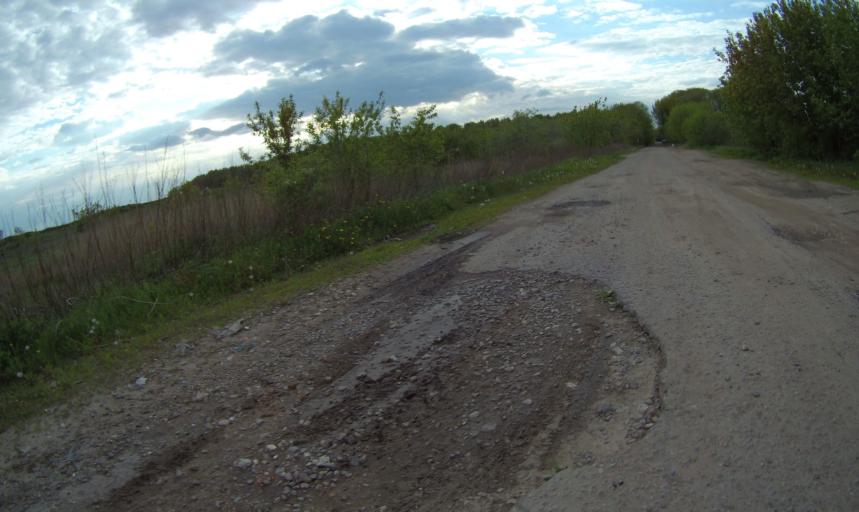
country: RU
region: Moskovskaya
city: Ramenskoye
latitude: 55.5631
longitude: 38.2787
